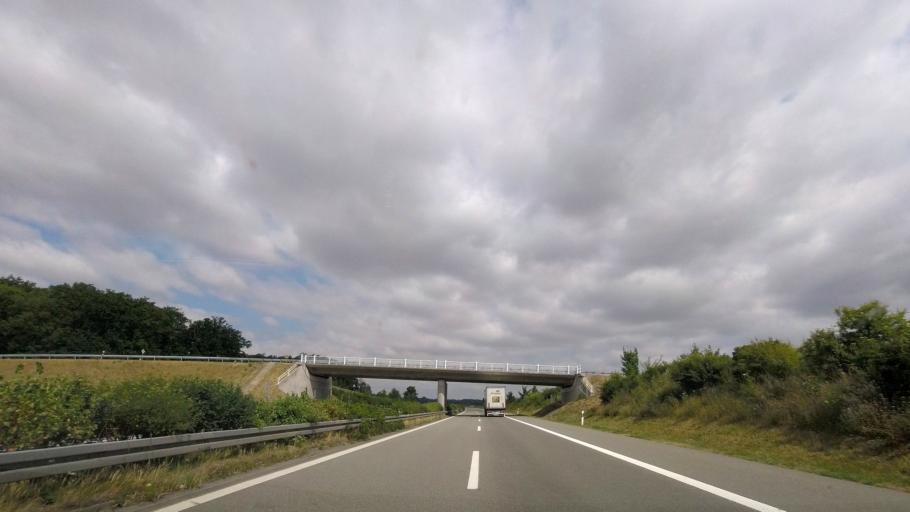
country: DE
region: Mecklenburg-Vorpommern
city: Jarmen
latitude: 53.9624
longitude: 13.3671
